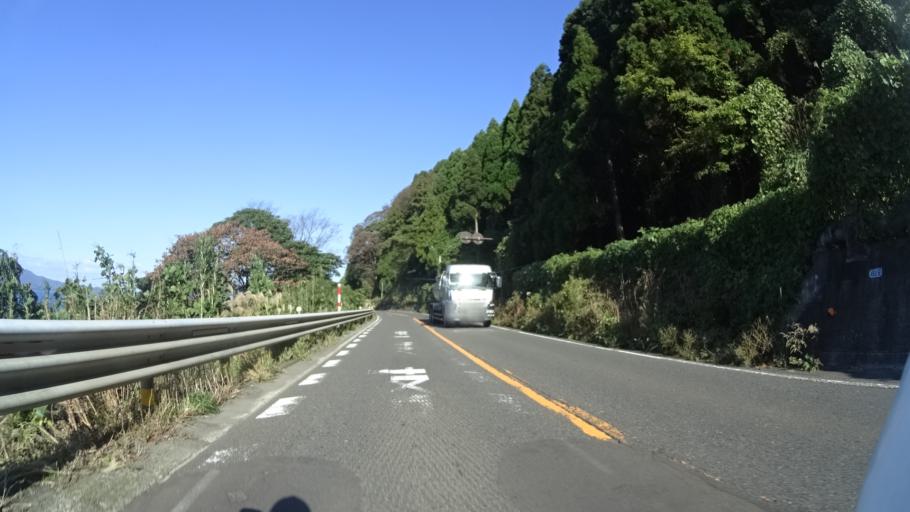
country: JP
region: Fukui
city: Tsuruga
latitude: 35.7281
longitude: 136.0981
